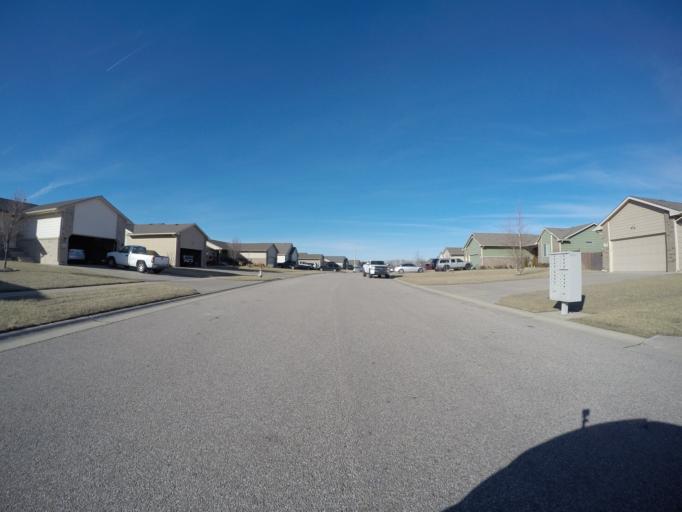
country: US
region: Kansas
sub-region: Sedgwick County
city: Goddard
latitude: 37.6540
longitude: -97.4838
